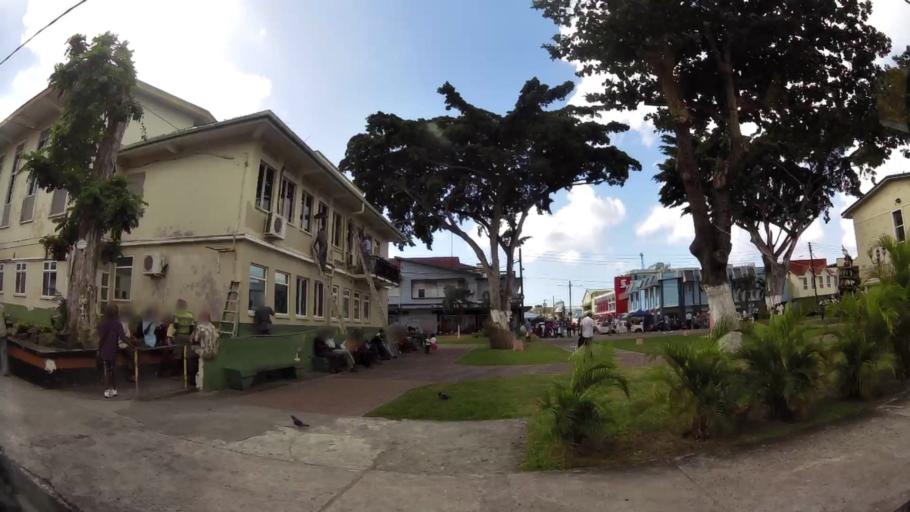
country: LC
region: Castries Quarter
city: Bisee
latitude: 14.0099
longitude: -60.9898
